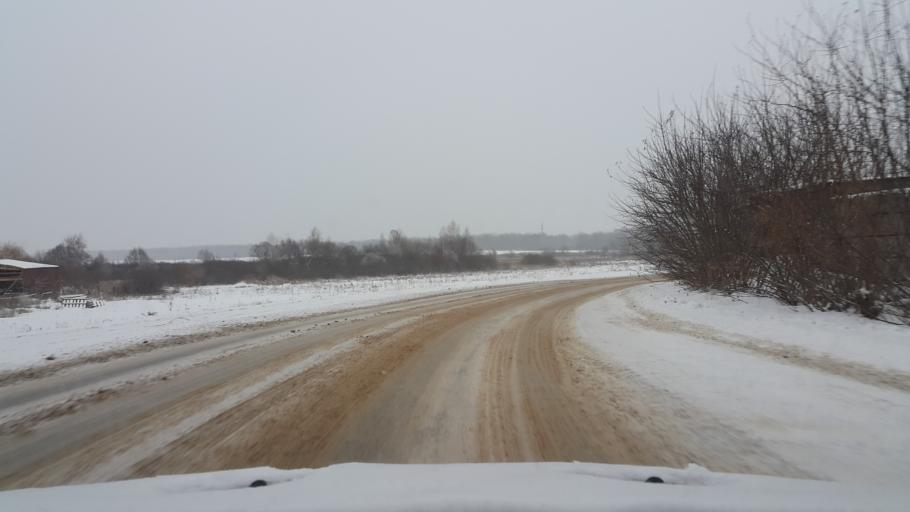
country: RU
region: Tambov
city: Pokrovo-Prigorodnoye
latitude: 52.6608
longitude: 41.4340
